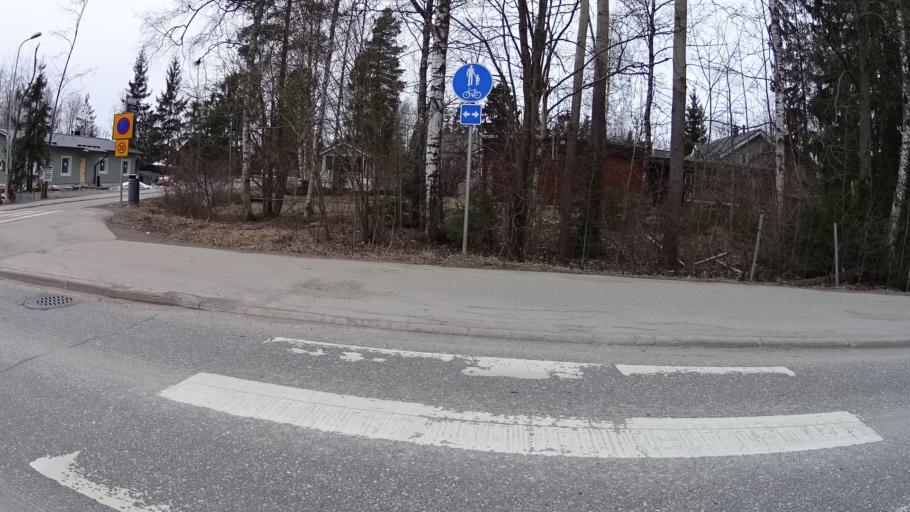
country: FI
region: Uusimaa
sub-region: Helsinki
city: Kauniainen
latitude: 60.2259
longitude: 24.7069
